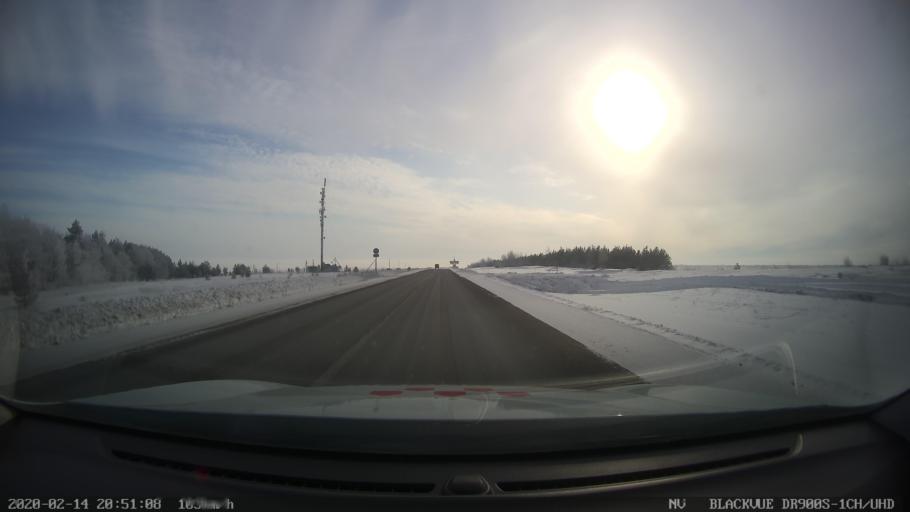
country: RU
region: Tatarstan
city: Kuybyshevskiy Zaton
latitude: 55.2165
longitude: 49.2342
